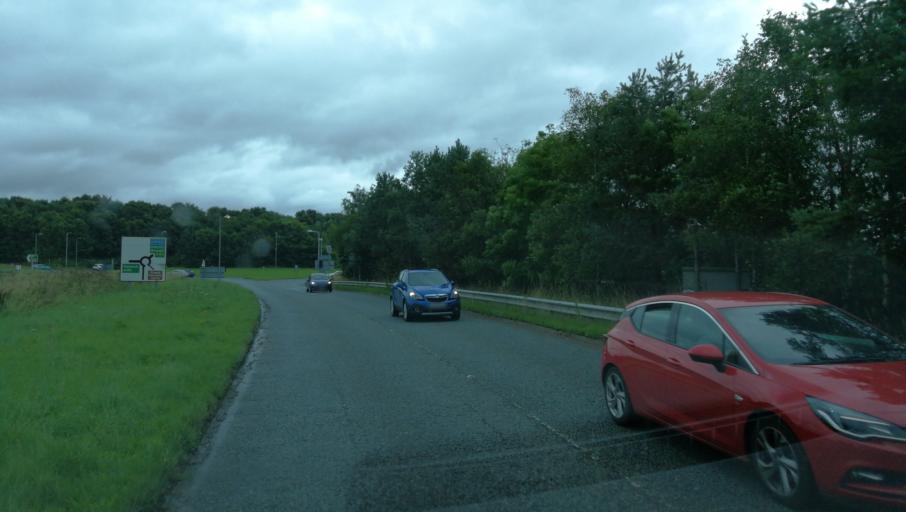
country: GB
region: England
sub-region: Cumbria
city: Penrith
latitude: 54.6467
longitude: -2.7820
